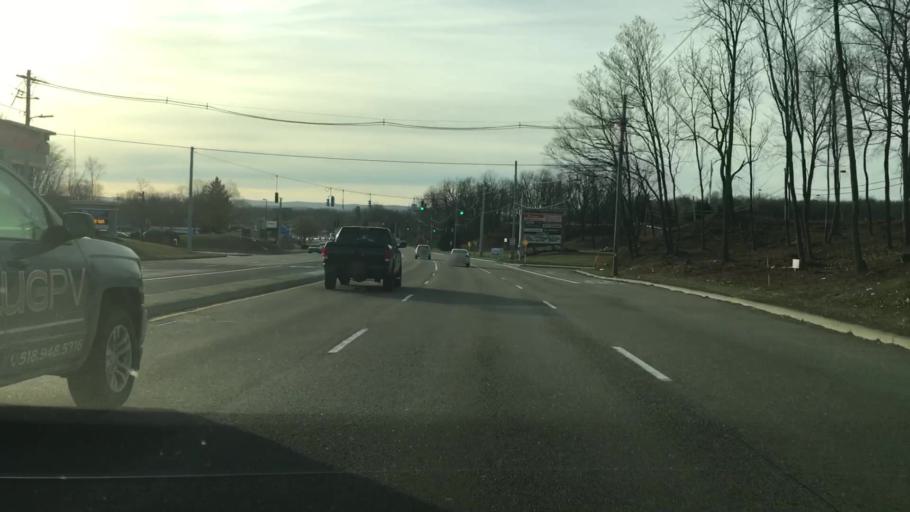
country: US
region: New York
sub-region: Dutchess County
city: Wappingers Falls
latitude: 41.6202
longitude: -73.9173
